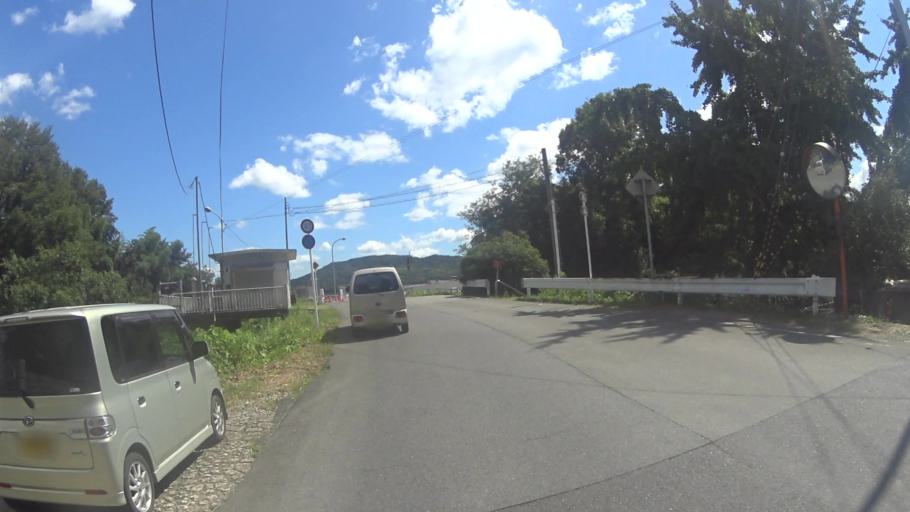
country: JP
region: Nara
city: Nara-shi
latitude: 34.7525
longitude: 135.8567
